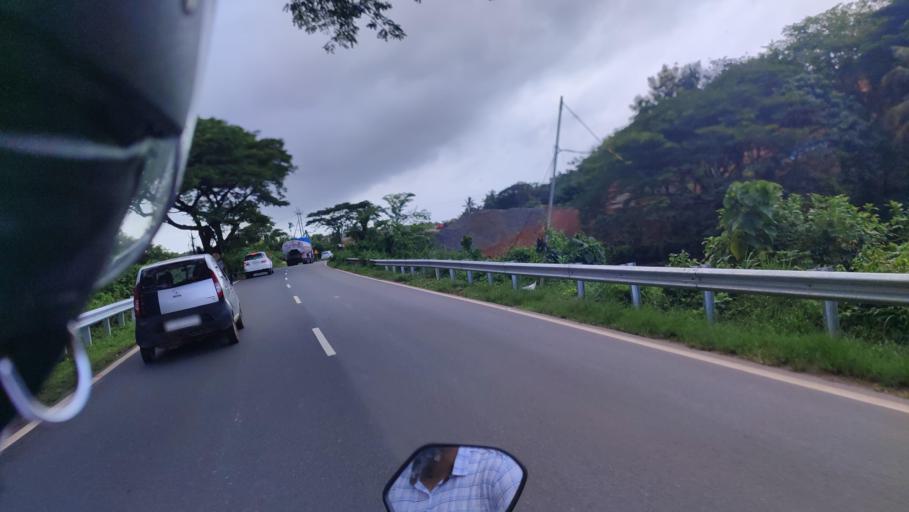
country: IN
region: Kerala
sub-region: Kasaragod District
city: Nileshwar
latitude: 12.2404
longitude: 75.1493
